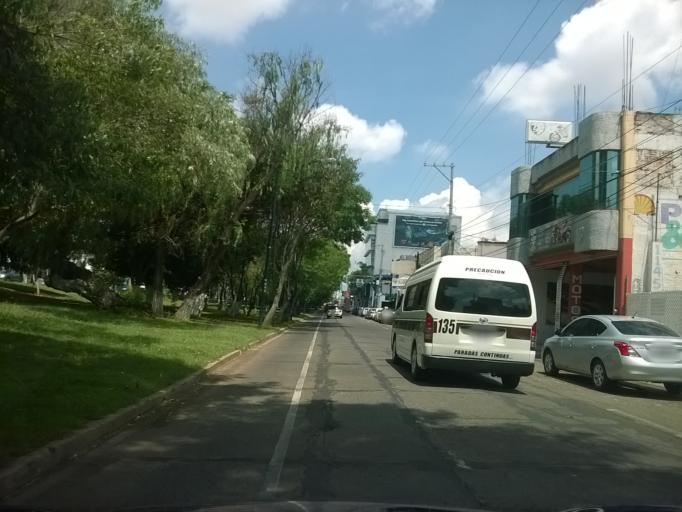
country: MX
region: Michoacan
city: Morelia
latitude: 19.6894
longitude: -101.1675
